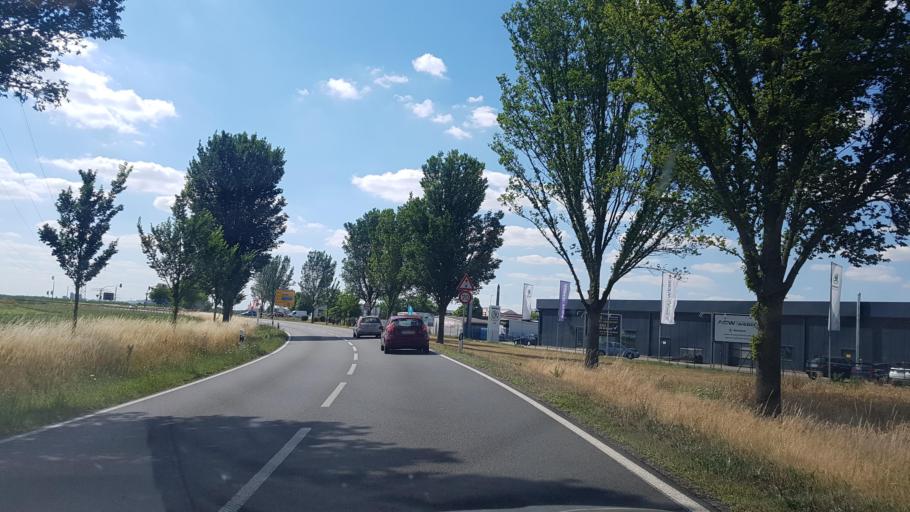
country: DE
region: Saxony
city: Dobernitz
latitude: 51.5100
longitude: 12.3407
